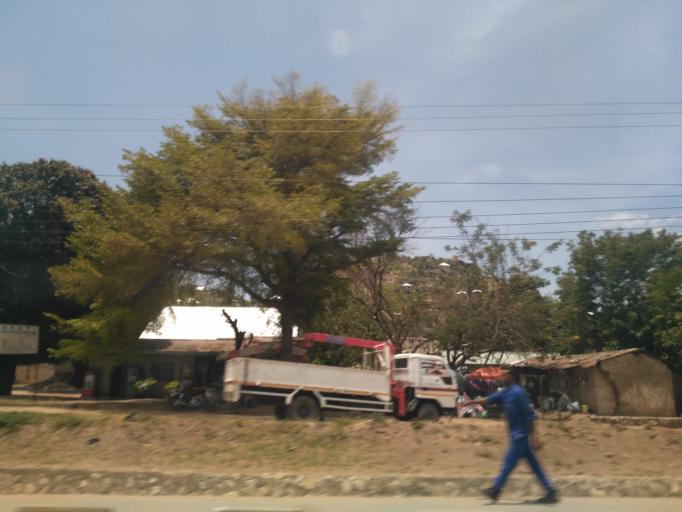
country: TZ
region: Mwanza
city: Mwanza
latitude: -2.5585
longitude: 32.9120
